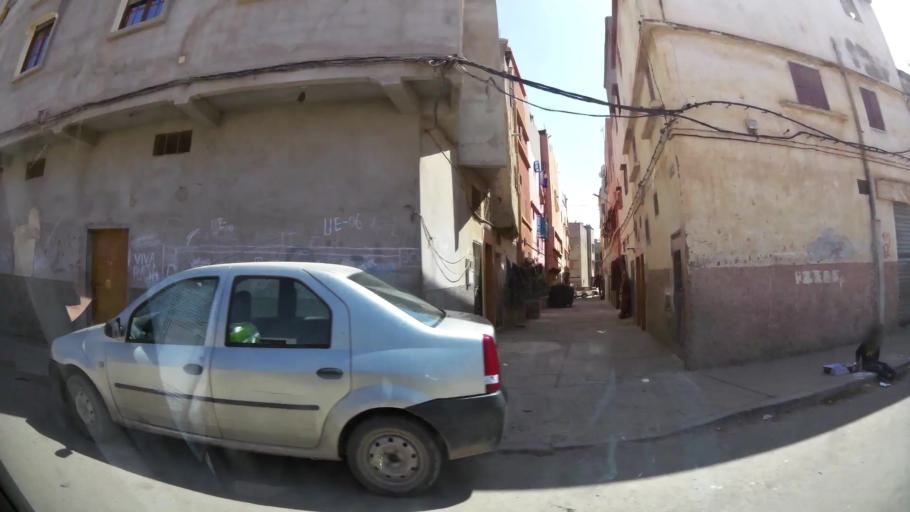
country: MA
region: Souss-Massa-Draa
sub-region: Inezgane-Ait Mellou
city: Inezgane
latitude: 30.3460
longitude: -9.5421
